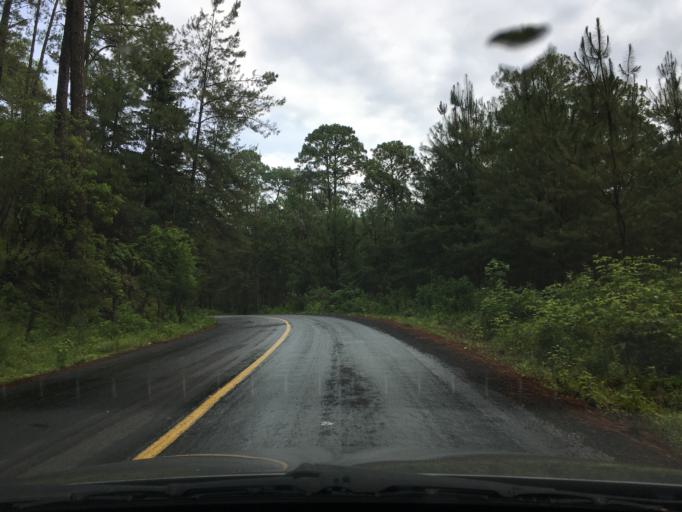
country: MX
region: Michoacan
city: Nuevo San Juan Parangaricutiro
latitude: 19.4394
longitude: -102.1501
